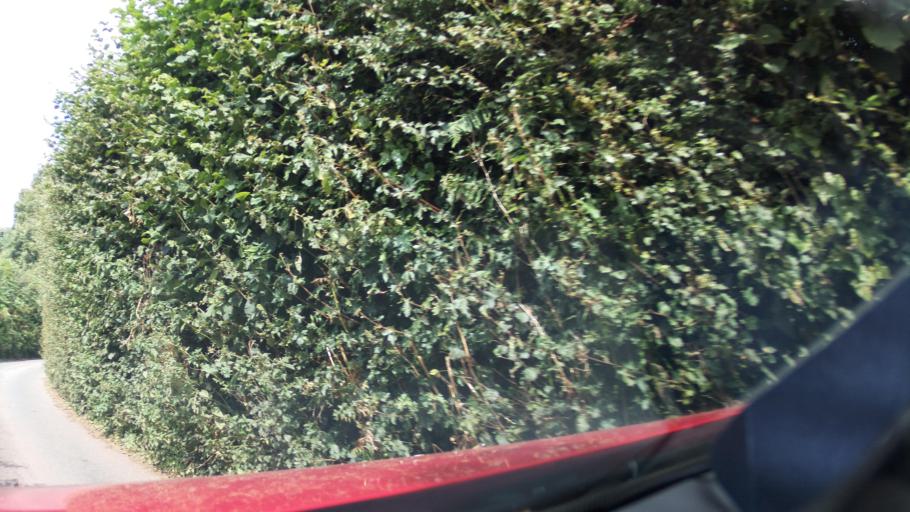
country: GB
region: England
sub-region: Devon
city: Marldon
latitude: 50.4169
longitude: -3.6256
